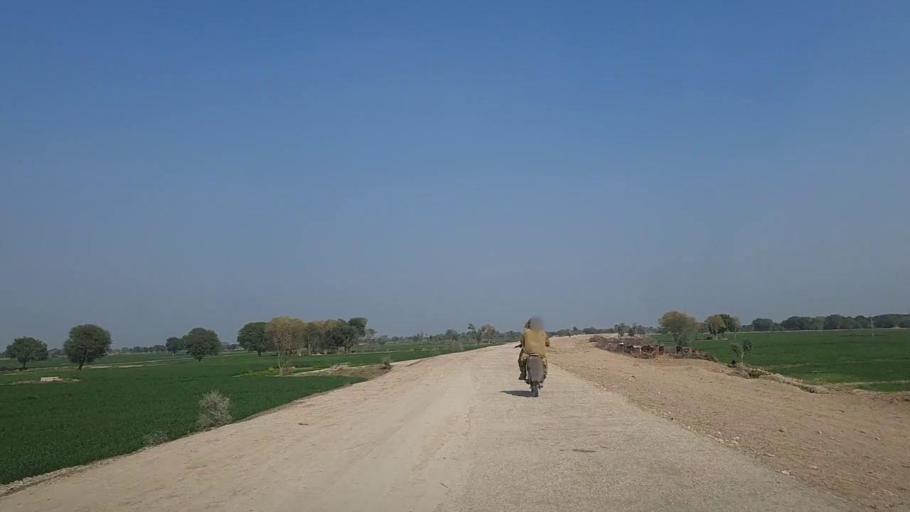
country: PK
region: Sindh
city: Moro
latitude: 26.7964
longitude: 67.9388
